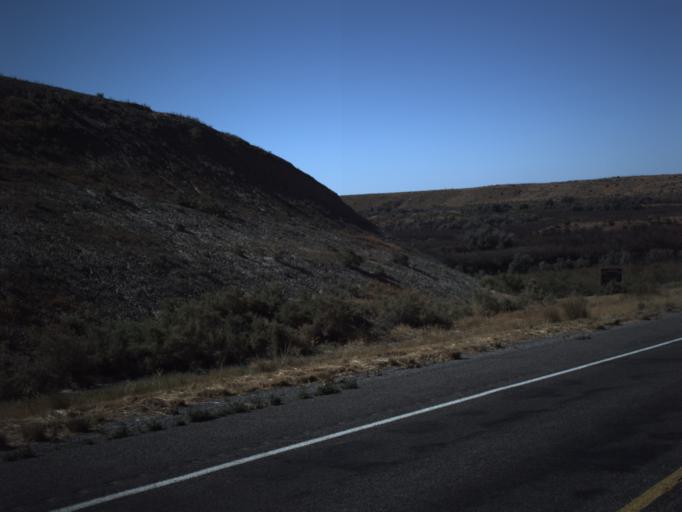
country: US
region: Utah
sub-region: Millard County
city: Delta
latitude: 39.4026
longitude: -112.4966
